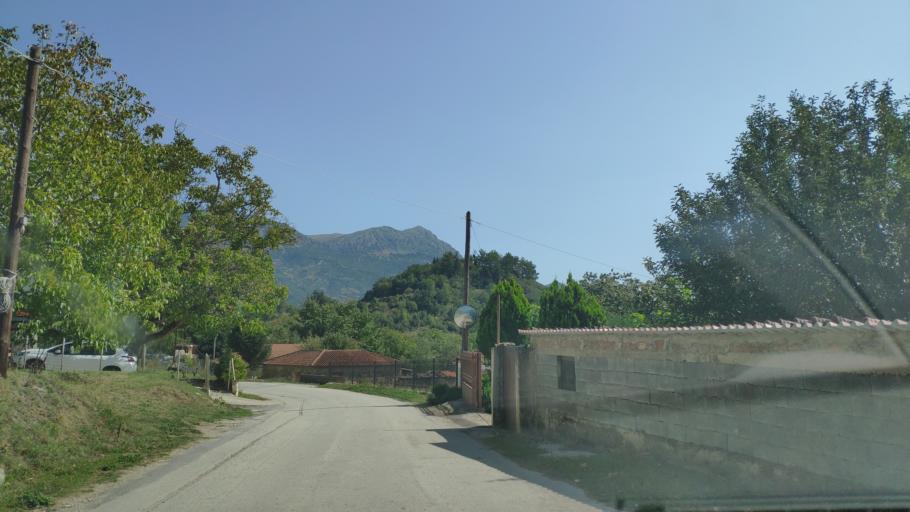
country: GR
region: West Greece
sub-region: Nomos Achaias
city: Kalavryta
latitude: 37.9129
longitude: 22.3012
